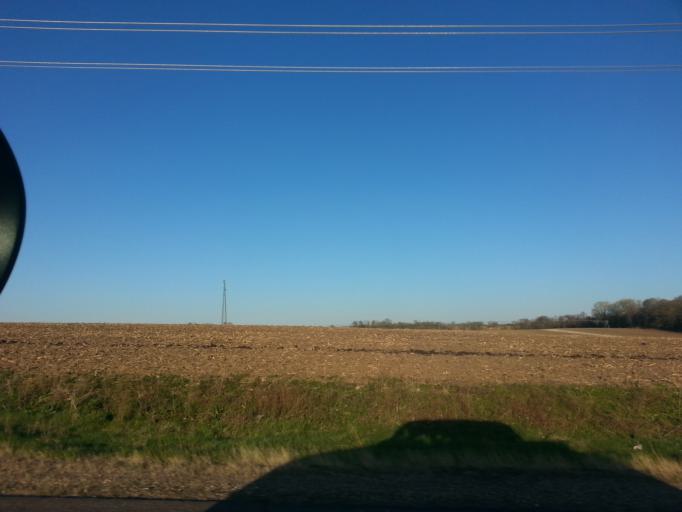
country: US
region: Wisconsin
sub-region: Pierce County
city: Prescott
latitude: 44.6133
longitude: -92.7724
